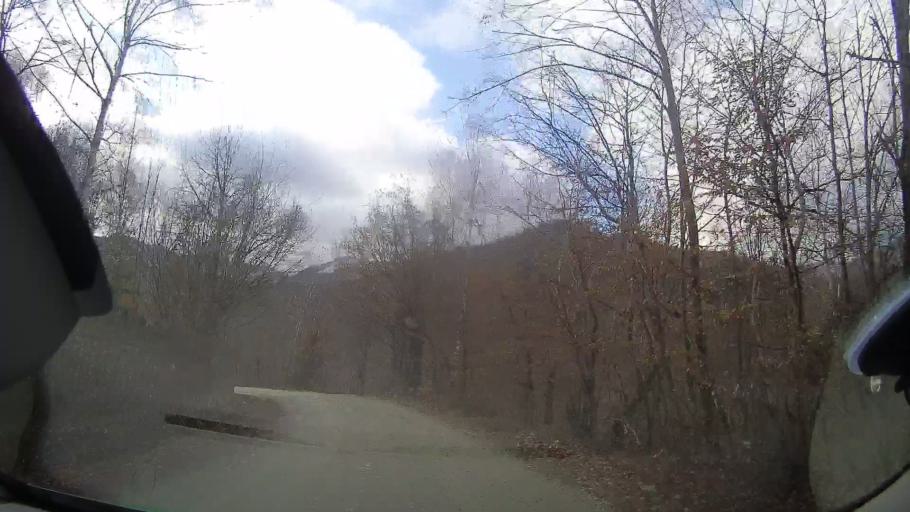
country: RO
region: Cluj
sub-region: Comuna Valea Ierii
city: Valea Ierii
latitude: 46.6867
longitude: 23.3097
